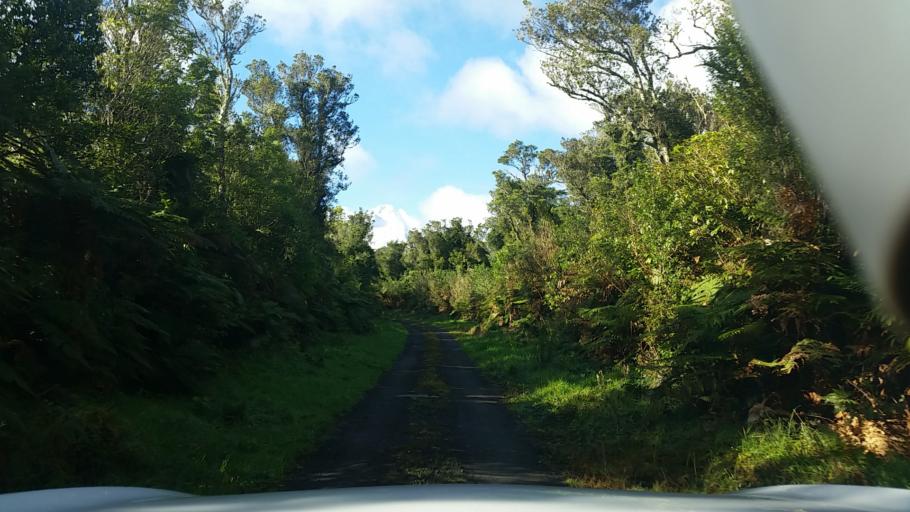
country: NZ
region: Taranaki
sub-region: South Taranaki District
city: Opunake
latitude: -39.2503
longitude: 173.9428
